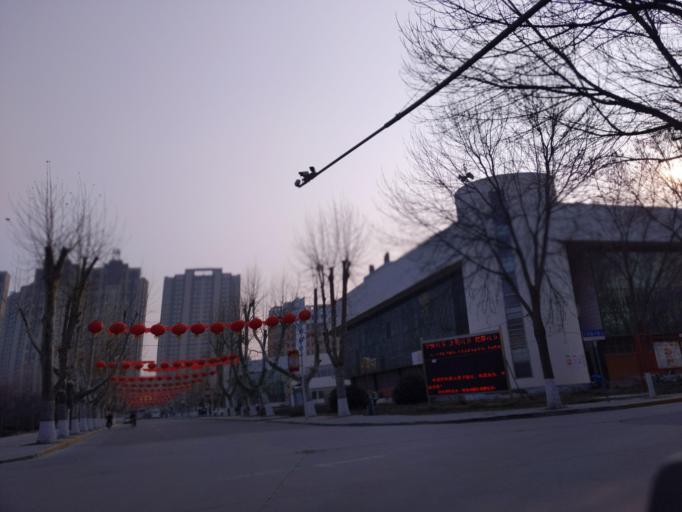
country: CN
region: Henan Sheng
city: Zhongyuanlu
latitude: 35.7811
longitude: 115.0567
